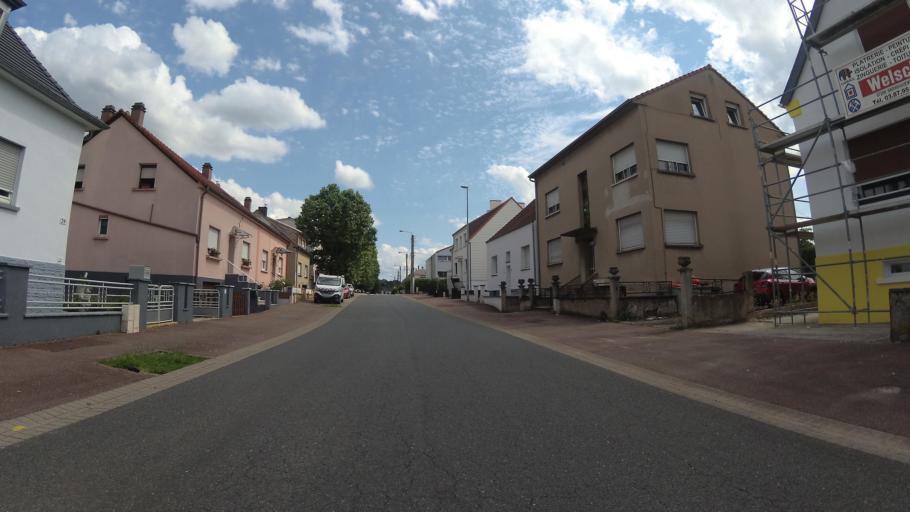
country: FR
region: Lorraine
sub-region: Departement de la Moselle
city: Sarreguemines
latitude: 49.1155
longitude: 7.0854
